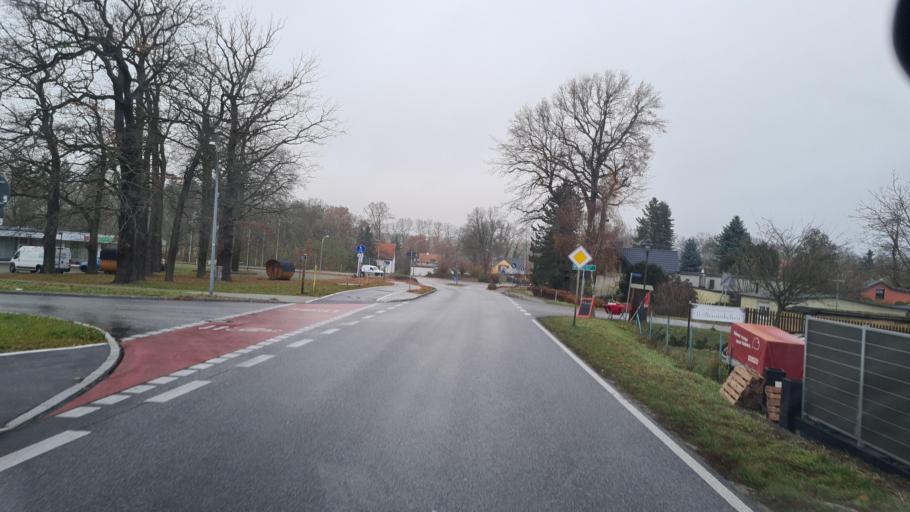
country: DE
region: Brandenburg
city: Gross Kreutz
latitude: 52.4028
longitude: 12.7708
